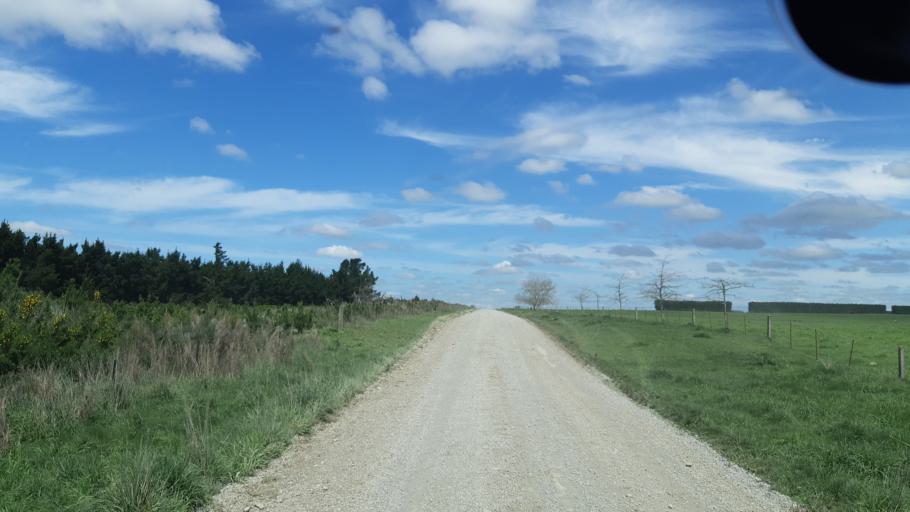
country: NZ
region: Canterbury
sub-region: Ashburton District
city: Methven
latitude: -43.6980
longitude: 171.4614
